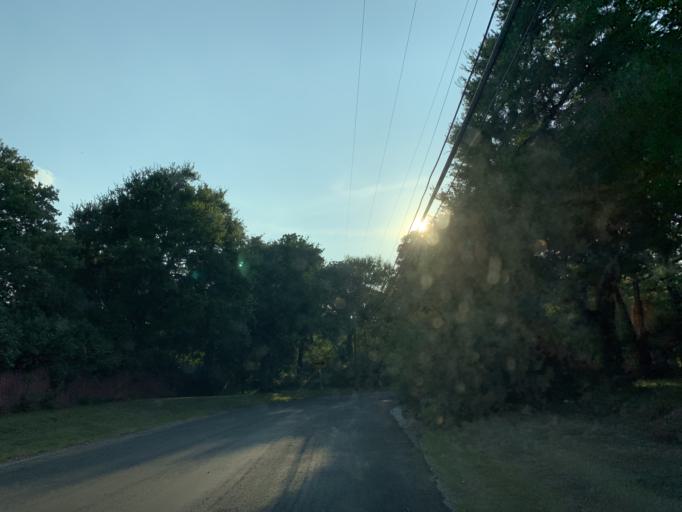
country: US
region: Texas
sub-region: Tarrant County
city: Richland Hills
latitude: 32.7791
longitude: -97.2003
